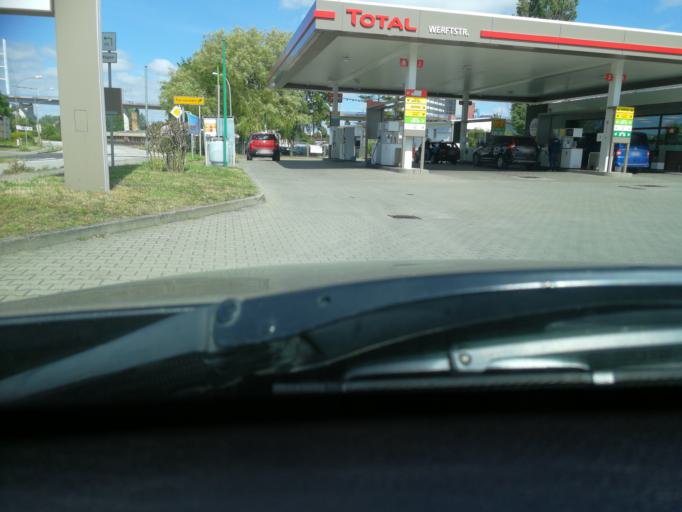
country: DE
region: Mecklenburg-Vorpommern
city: Stralsund
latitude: 54.3022
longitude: 13.1000
